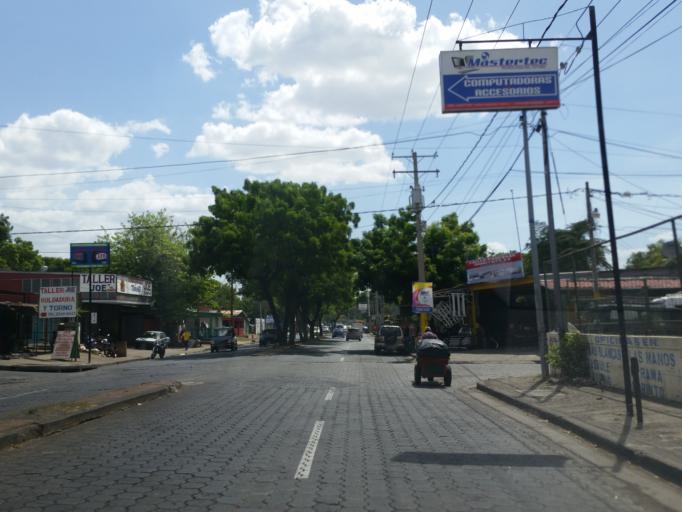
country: NI
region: Managua
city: Managua
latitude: 12.1463
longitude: -86.2446
